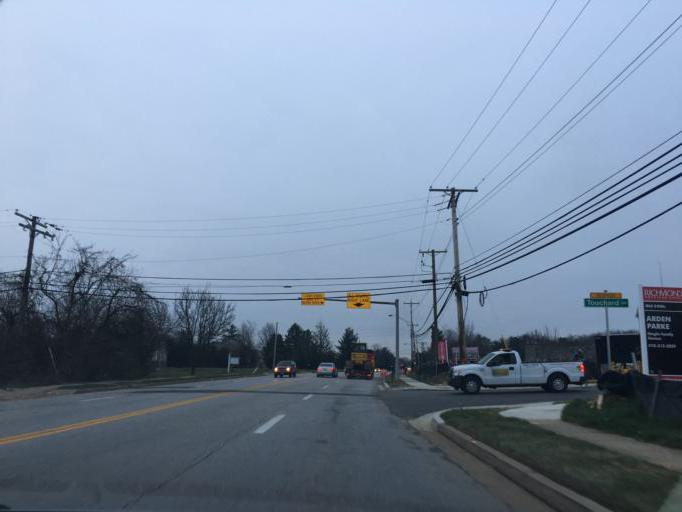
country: US
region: Maryland
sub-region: Baltimore County
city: Woodlawn
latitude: 39.3024
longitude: -76.7539
